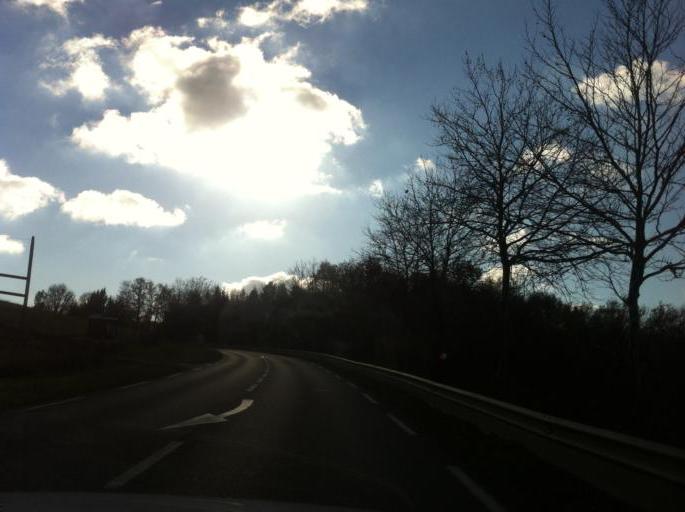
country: FR
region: Aquitaine
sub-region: Departement de la Dordogne
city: Rouffignac-Saint-Cernin-de-Reilhac
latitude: 45.0610
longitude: 0.8627
